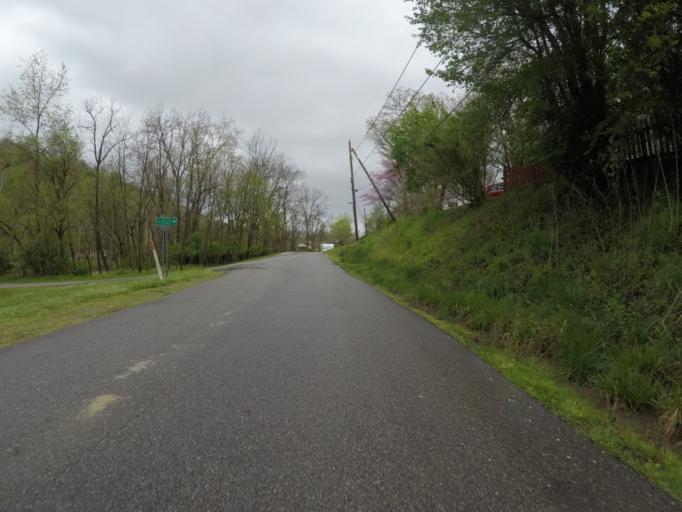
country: US
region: Ohio
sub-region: Lawrence County
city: Burlington
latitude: 38.3733
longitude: -82.5055
